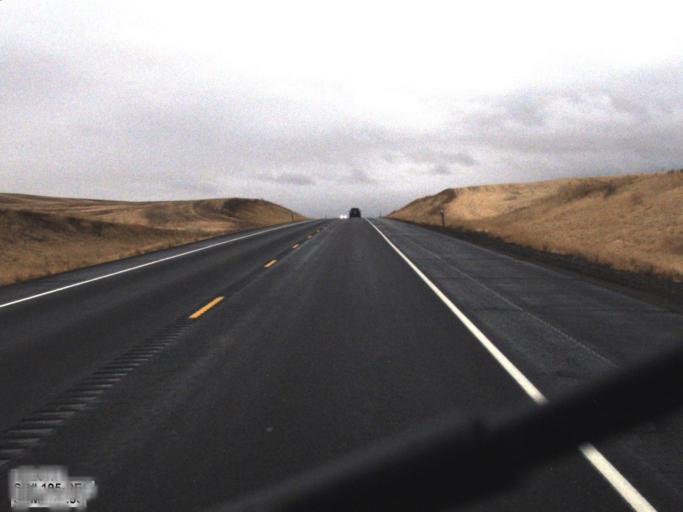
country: US
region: Washington
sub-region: Spokane County
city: Cheney
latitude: 47.4048
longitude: -117.3916
